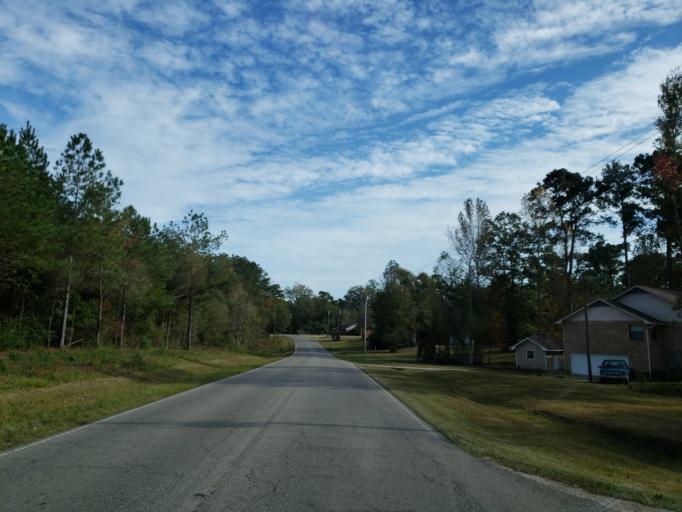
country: US
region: Mississippi
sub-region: Lamar County
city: West Hattiesburg
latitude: 31.3051
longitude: -89.3854
